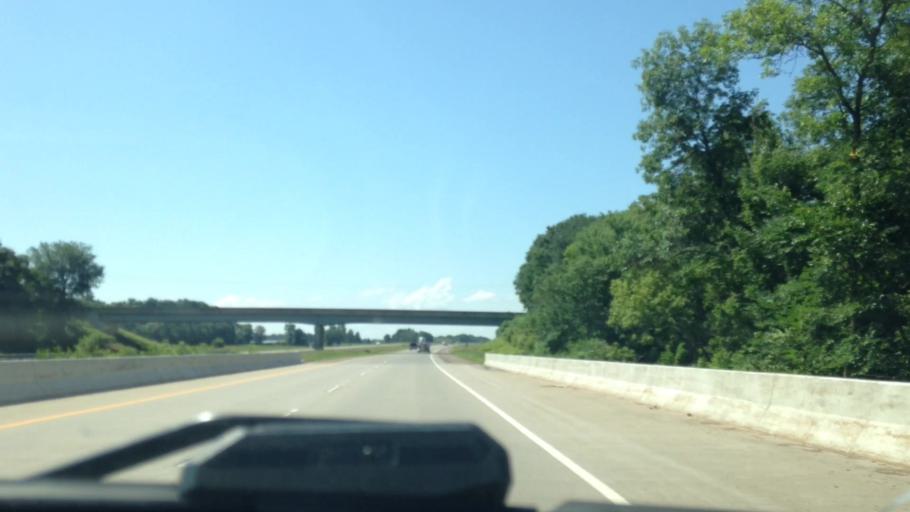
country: US
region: Wisconsin
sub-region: Barron County
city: Cameron
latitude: 45.4462
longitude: -91.7598
